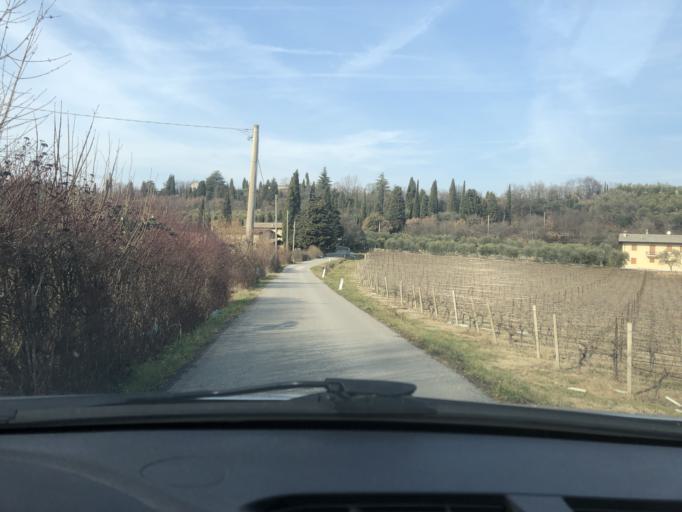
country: IT
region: Veneto
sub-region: Provincia di Verona
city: Costermano
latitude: 45.5684
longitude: 10.7334
